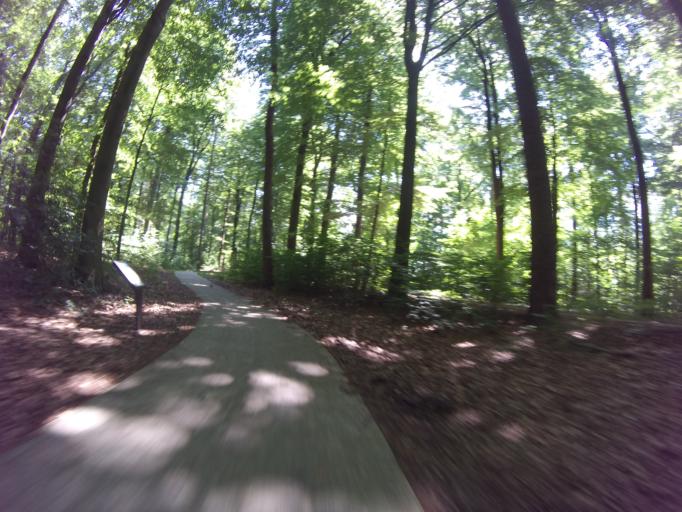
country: NL
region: Drenthe
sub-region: Gemeente Emmen
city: Emmen
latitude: 52.7883
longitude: 6.9153
